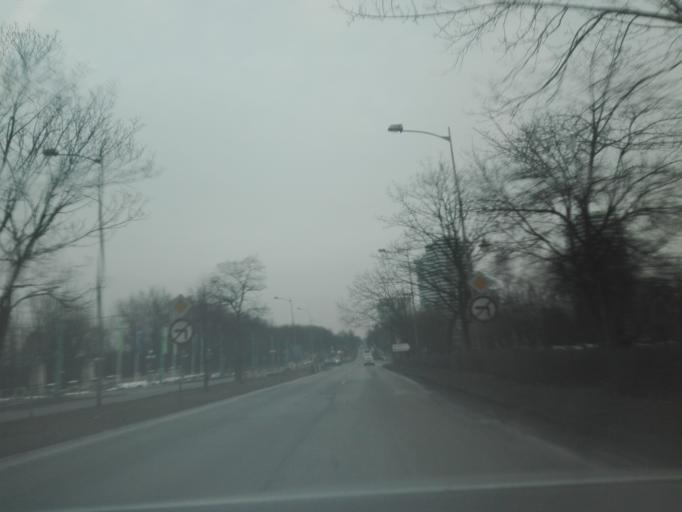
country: PL
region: Silesian Voivodeship
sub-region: Chorzow
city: Chorzow
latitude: 50.2831
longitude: 18.9745
